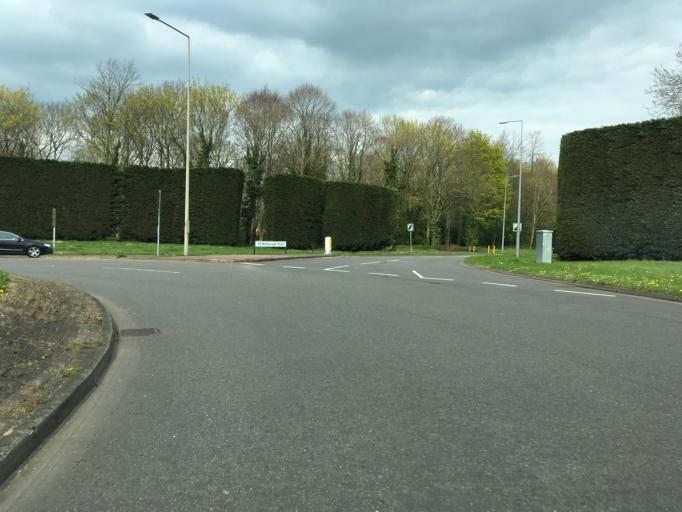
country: GB
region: England
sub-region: Milton Keynes
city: Bradwell
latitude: 52.0668
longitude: -0.7759
